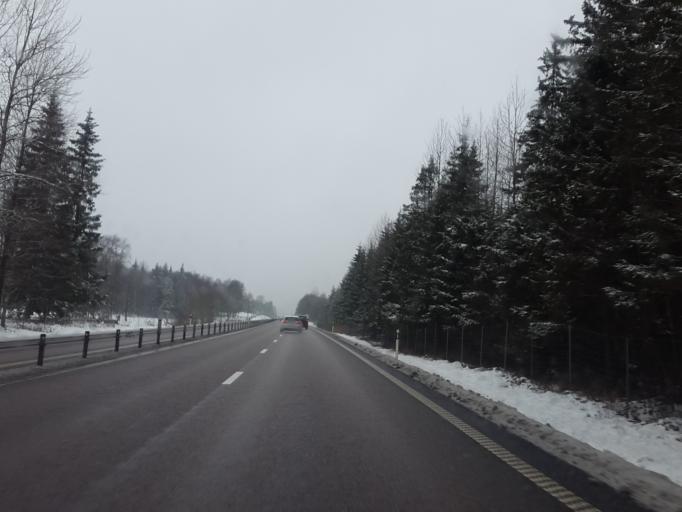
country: SE
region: Vaestra Goetaland
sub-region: Ulricehamns Kommun
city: Ulricehamn
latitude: 57.7968
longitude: 13.5776
